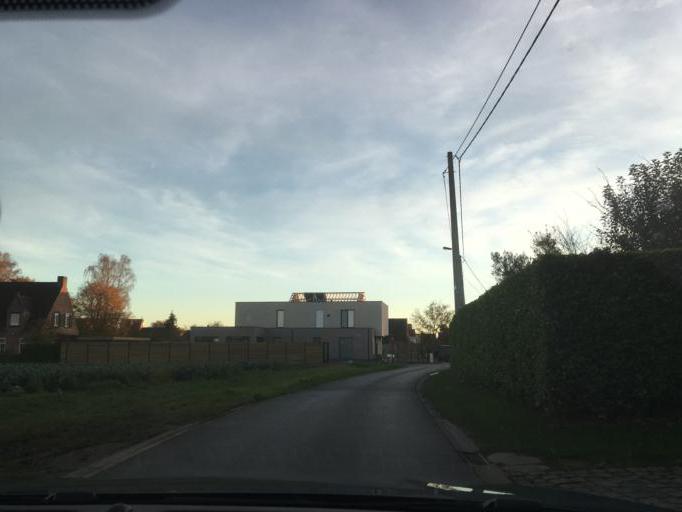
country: BE
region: Flanders
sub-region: Provincie West-Vlaanderen
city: Ardooie
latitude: 50.9792
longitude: 3.2102
